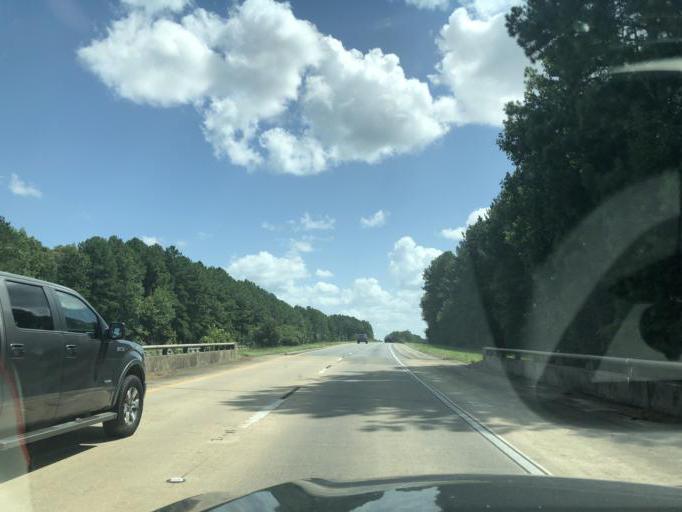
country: US
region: Georgia
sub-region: Troup County
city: La Grange
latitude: 33.0210
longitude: -84.9523
